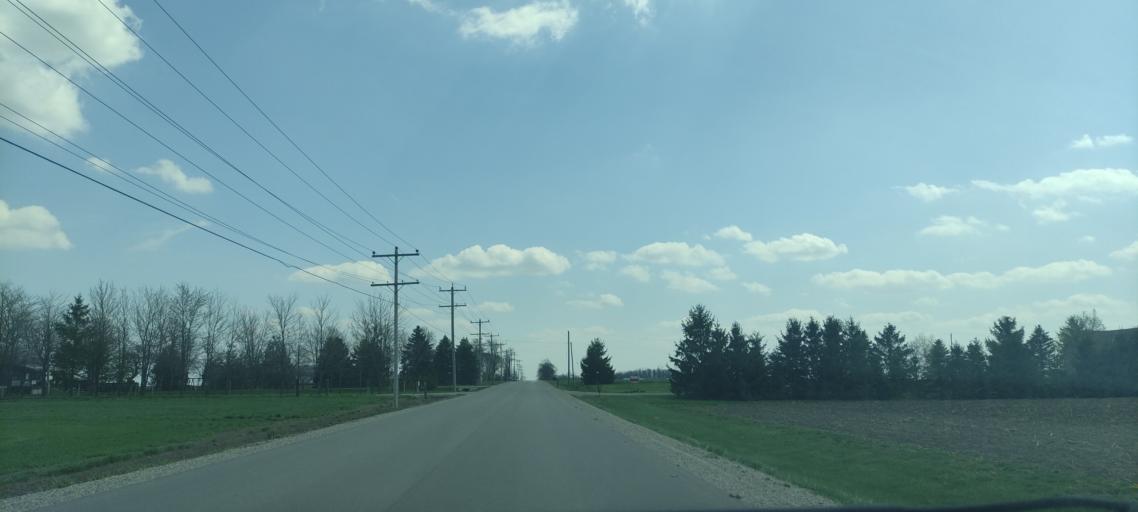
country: CA
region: Ontario
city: Stratford
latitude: 43.3332
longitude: -80.9041
